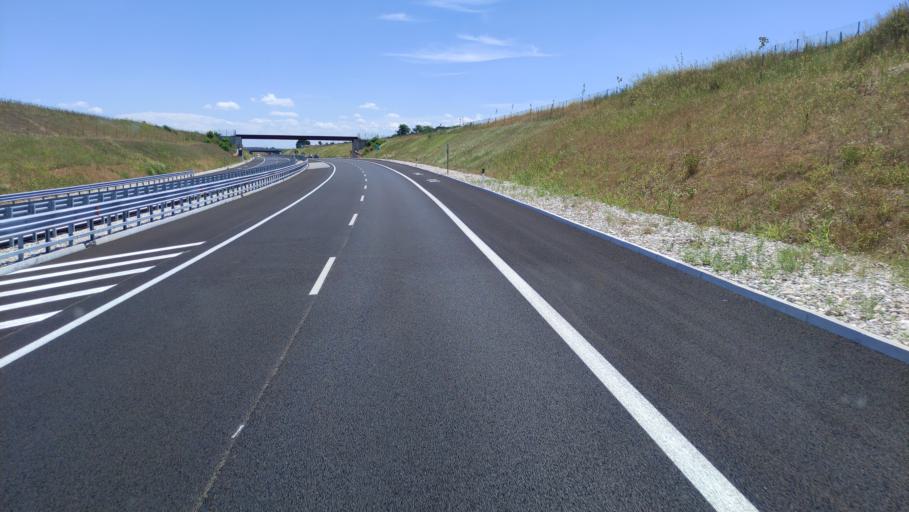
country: IT
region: Veneto
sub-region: Provincia di Treviso
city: San Vito
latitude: 45.7453
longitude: 11.9193
